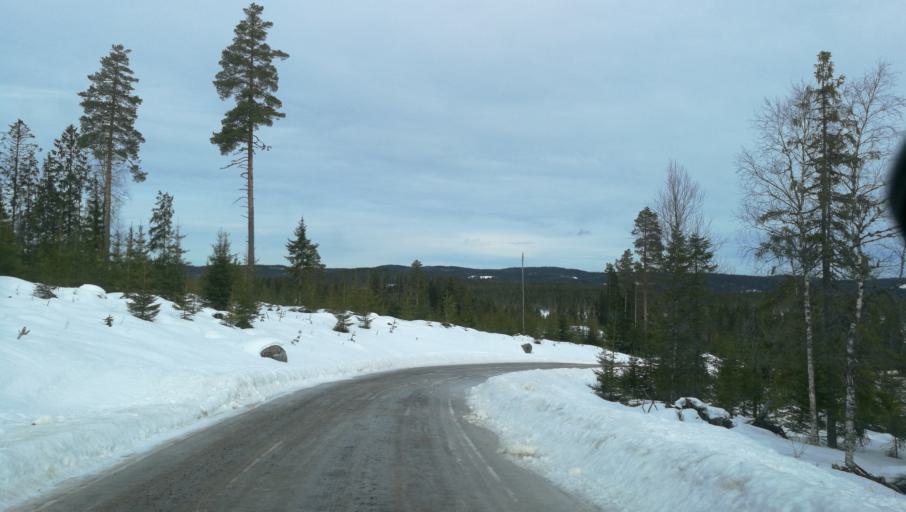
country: SE
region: Vaermland
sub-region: Torsby Kommun
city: Torsby
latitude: 60.6639
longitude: 12.8307
